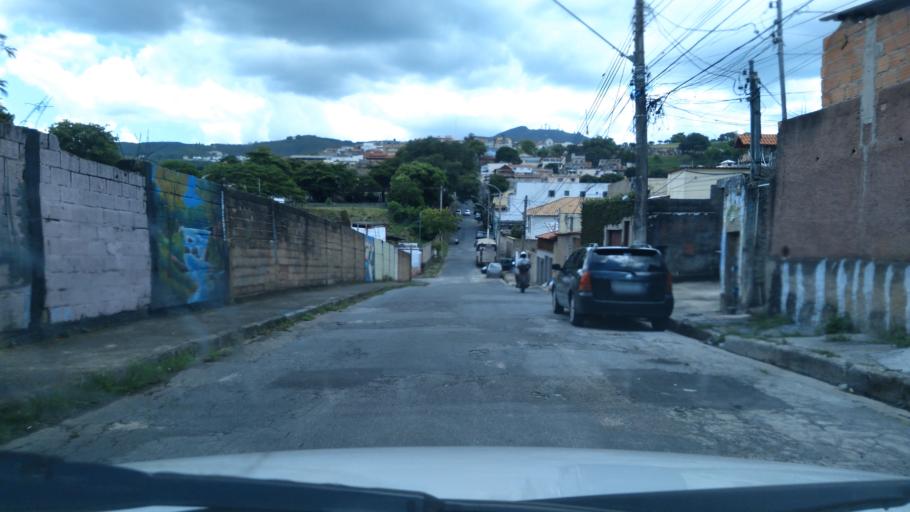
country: BR
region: Minas Gerais
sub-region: Belo Horizonte
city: Belo Horizonte
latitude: -19.9124
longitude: -43.8956
